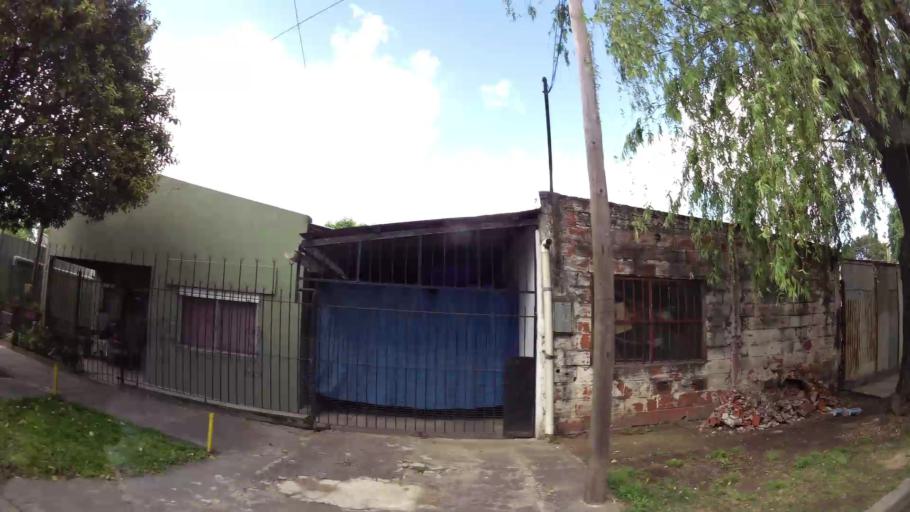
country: AR
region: Buenos Aires
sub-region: Partido de Quilmes
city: Quilmes
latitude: -34.8343
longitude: -58.1897
